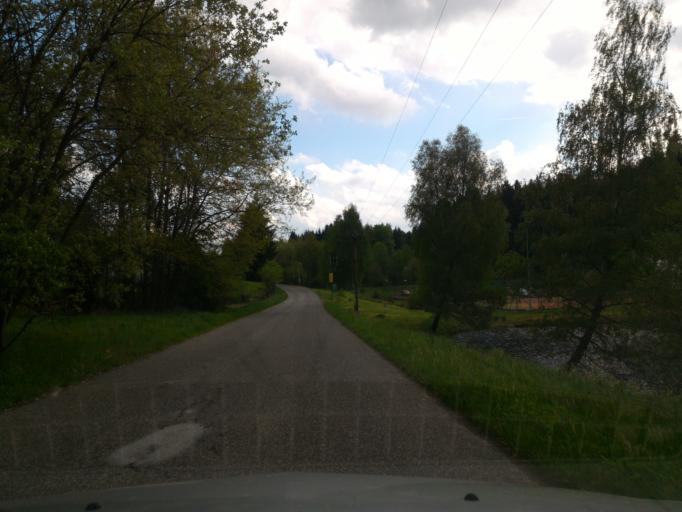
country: CZ
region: Vysocina
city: Ledec nad Sazavou
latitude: 49.6392
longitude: 15.3004
